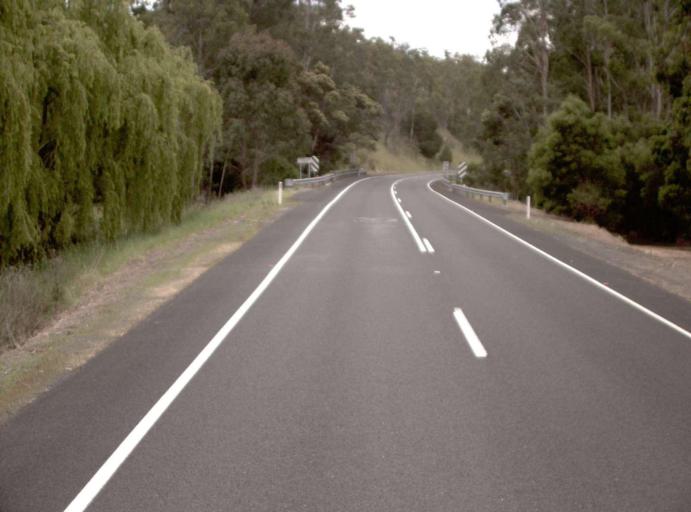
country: AU
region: New South Wales
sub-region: Bombala
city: Bombala
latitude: -37.3330
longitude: 149.2059
